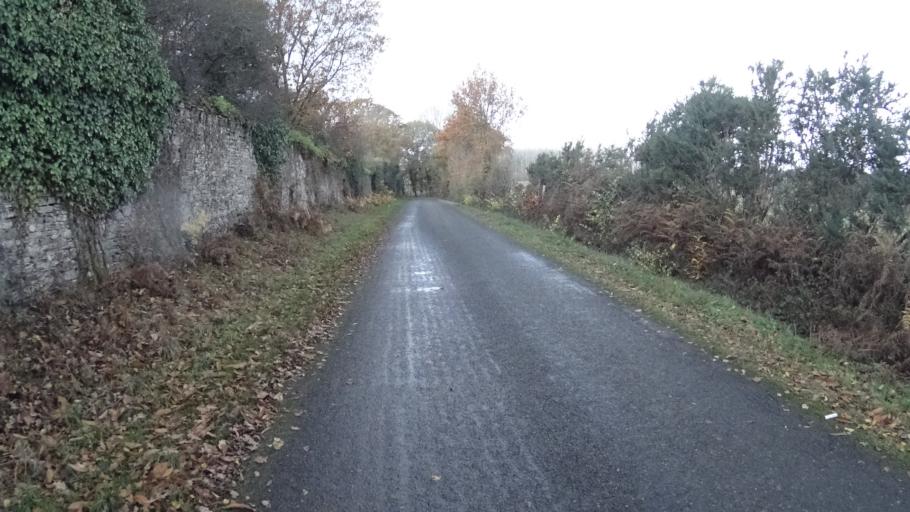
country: FR
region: Pays de la Loire
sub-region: Departement de la Loire-Atlantique
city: Avessac
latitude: 47.6658
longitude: -2.0051
